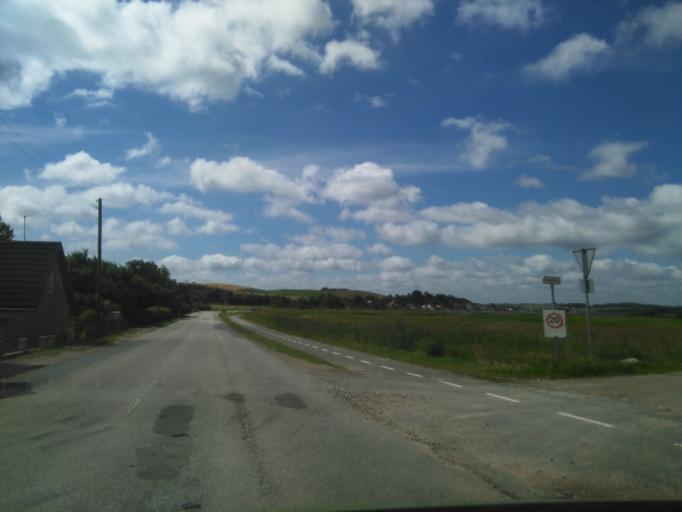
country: DK
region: Central Jutland
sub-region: Syddjurs Kommune
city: Ronde
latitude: 56.2098
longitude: 10.4846
